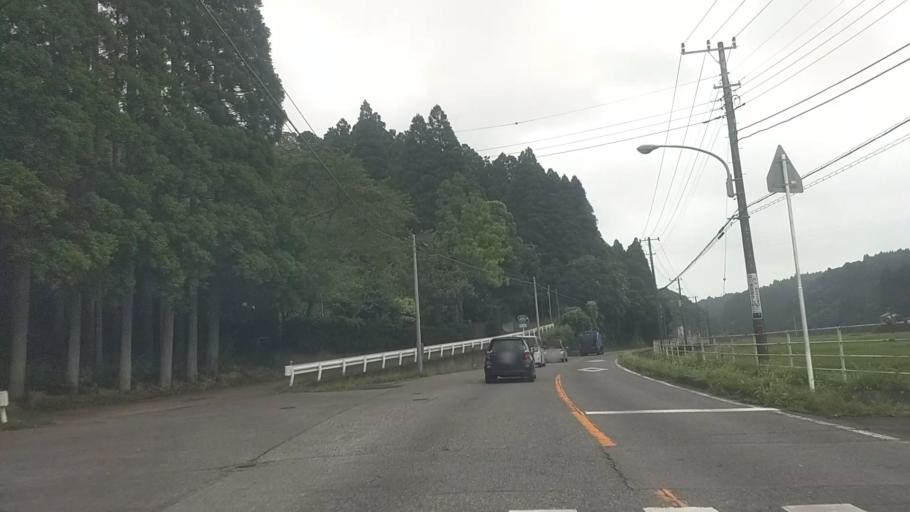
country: JP
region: Chiba
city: Ohara
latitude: 35.2649
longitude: 140.3557
